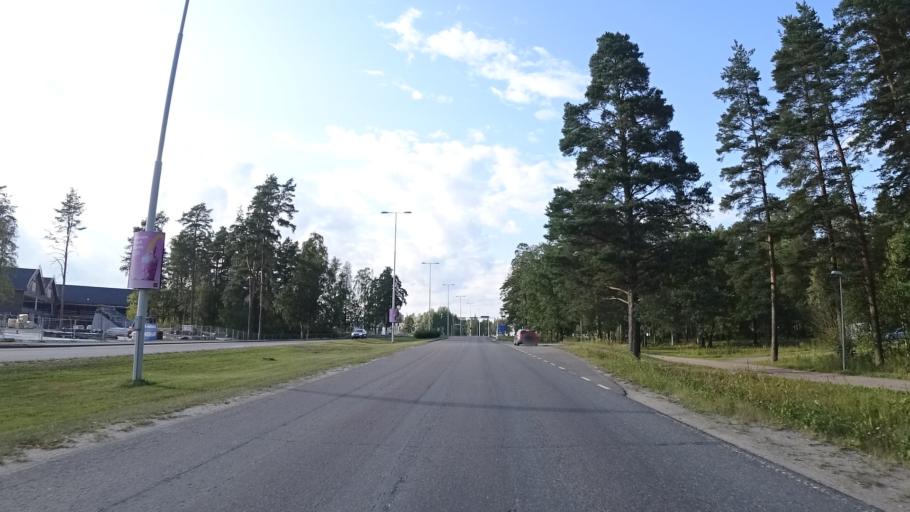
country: FI
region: South Karelia
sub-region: Imatra
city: Imatra
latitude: 61.1828
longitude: 28.7805
